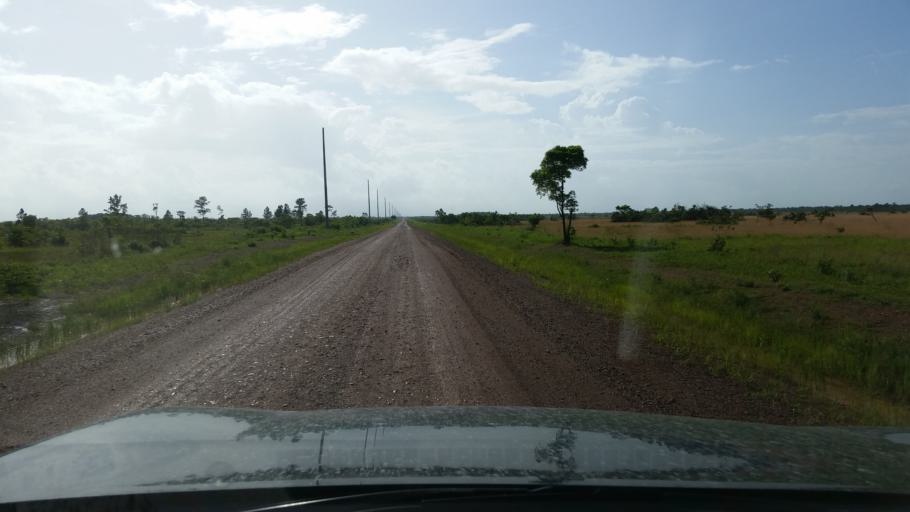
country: NI
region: Atlantico Norte (RAAN)
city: Puerto Cabezas
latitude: 14.1101
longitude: -83.6075
